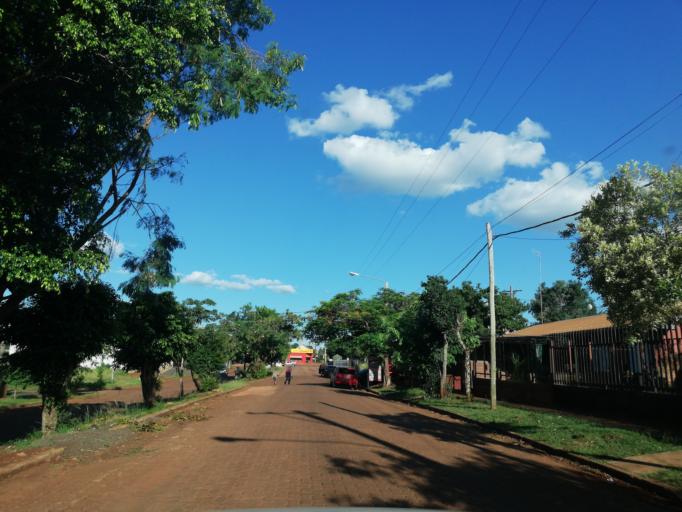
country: AR
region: Misiones
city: Garupa
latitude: -27.4666
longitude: -55.8648
